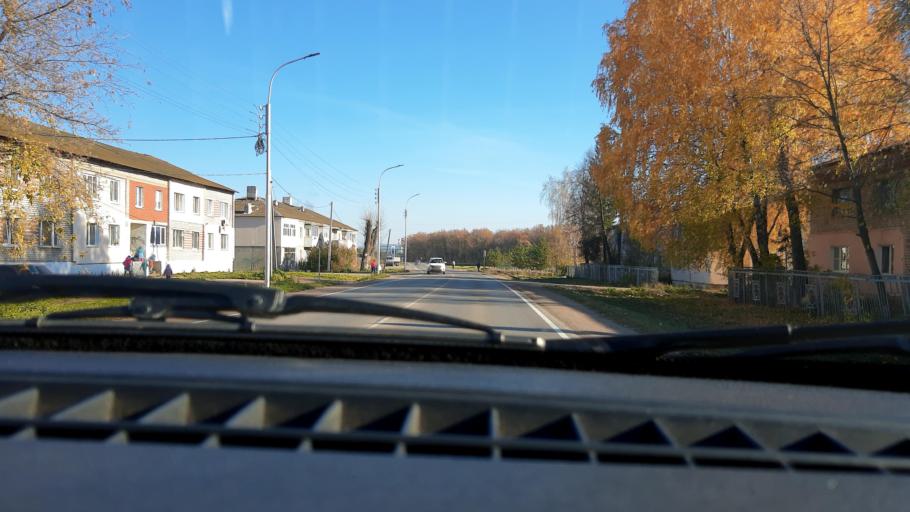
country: RU
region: Bashkortostan
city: Mikhaylovka
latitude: 54.8109
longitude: 55.8097
